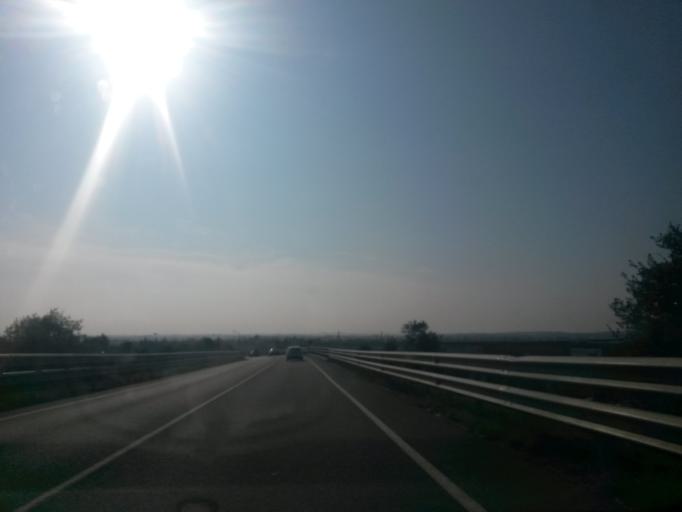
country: ES
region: Catalonia
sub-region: Provincia de Girona
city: Vilajuiga
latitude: 42.3264
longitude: 3.0893
